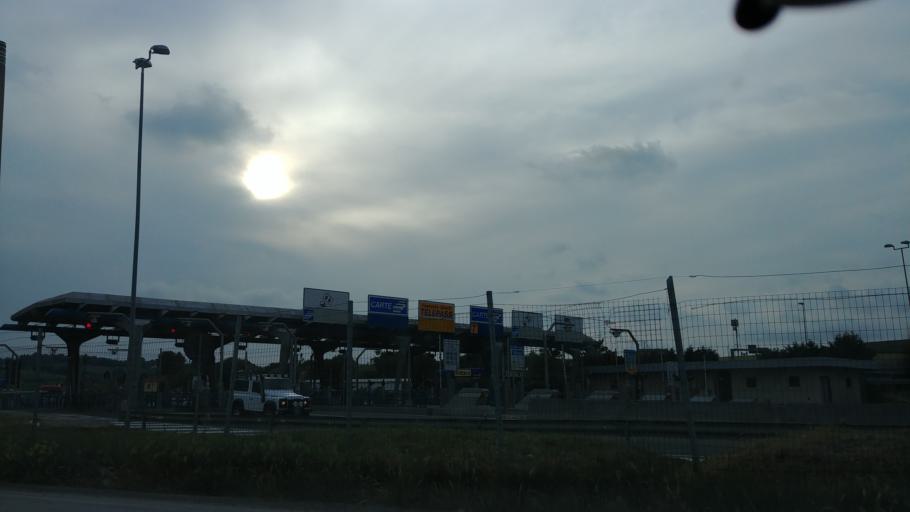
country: IT
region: The Marches
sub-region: Provincia di Pesaro e Urbino
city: Villa Ceccolini
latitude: 43.8972
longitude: 12.8422
